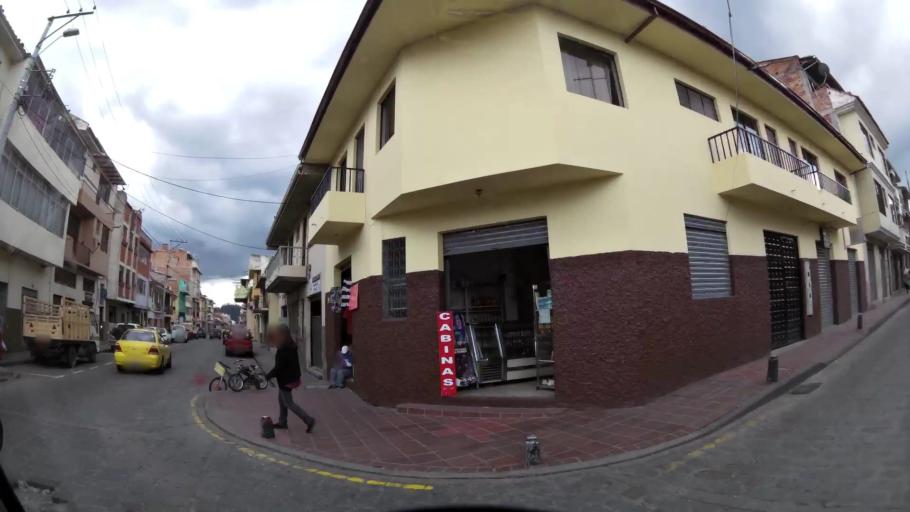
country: EC
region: Azuay
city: Cuenca
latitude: -2.8923
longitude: -79.0102
